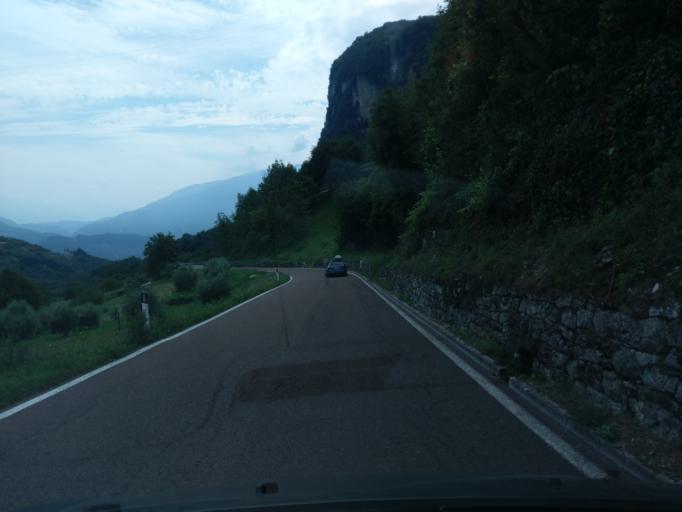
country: IT
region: Trentino-Alto Adige
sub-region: Provincia di Trento
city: Tenno
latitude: 45.9207
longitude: 10.8224
